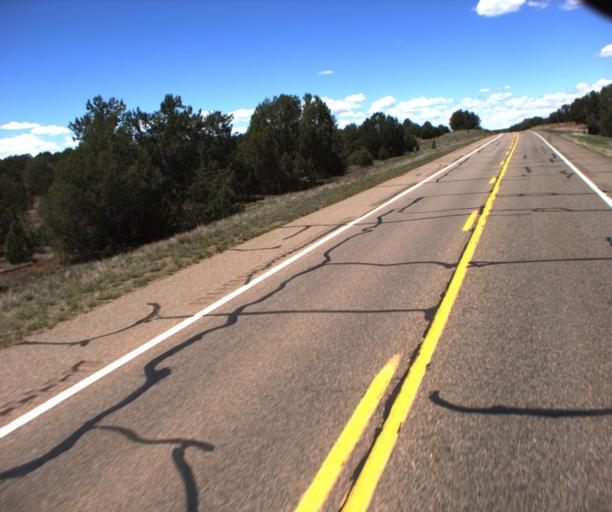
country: US
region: Arizona
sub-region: Yavapai County
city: Paulden
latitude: 35.1353
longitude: -112.4406
